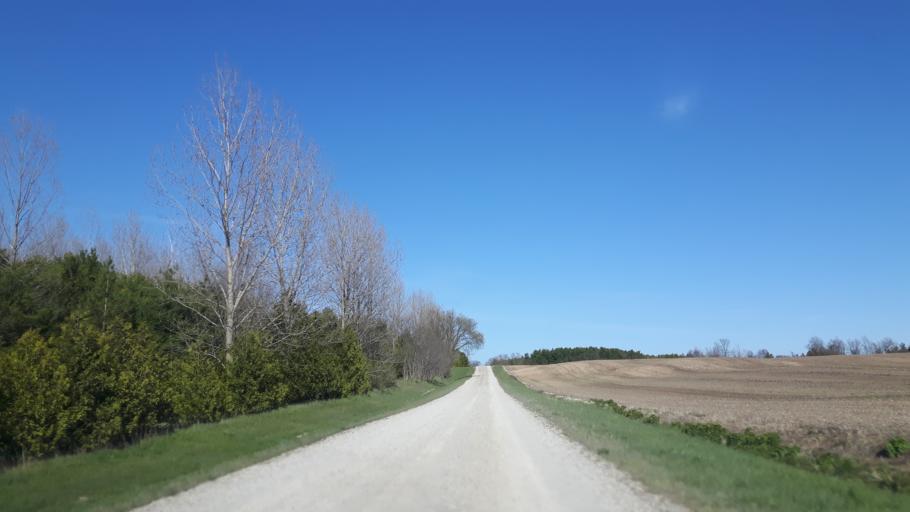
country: CA
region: Ontario
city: Goderich
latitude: 43.6614
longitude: -81.6708
